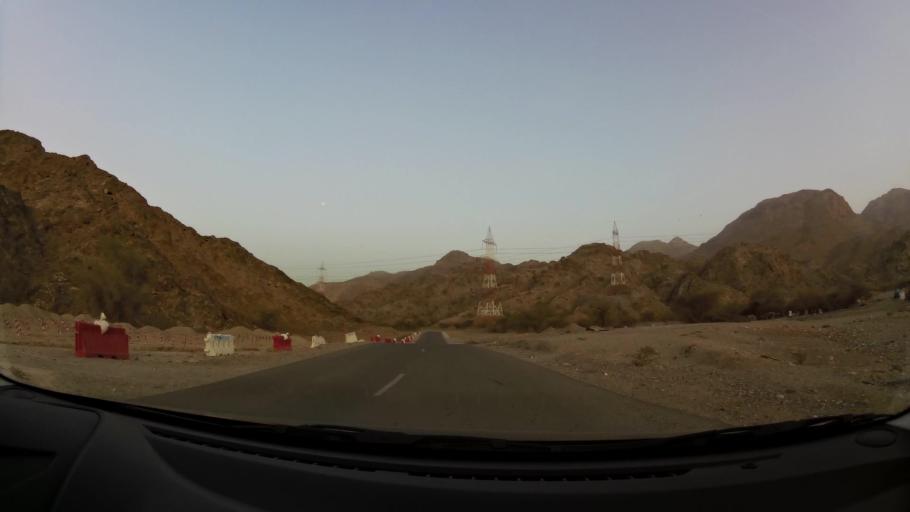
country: OM
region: Muhafazat Masqat
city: Bawshar
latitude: 23.4715
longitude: 58.3112
